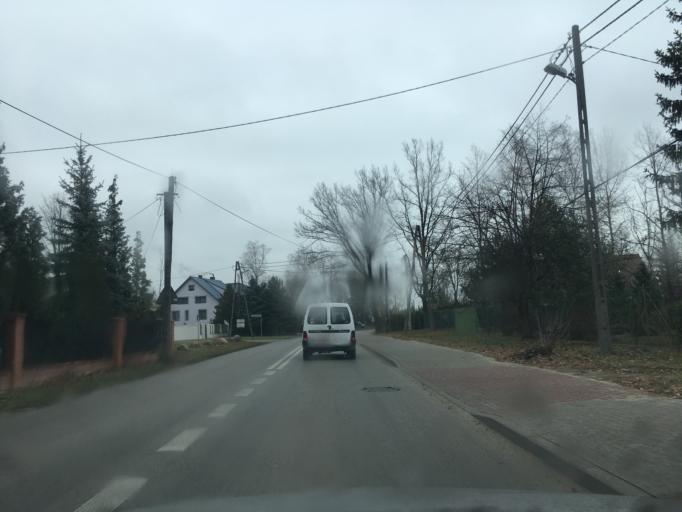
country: PL
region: Masovian Voivodeship
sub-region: Powiat piaseczynski
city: Lesznowola
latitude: 52.0640
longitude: 20.9221
